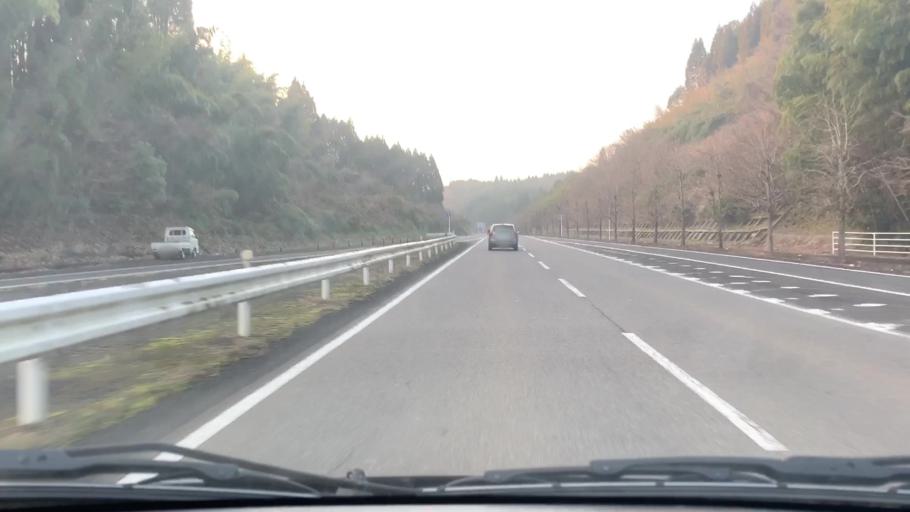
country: JP
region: Saga Prefecture
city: Imaricho-ko
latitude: 33.2649
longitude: 129.9582
